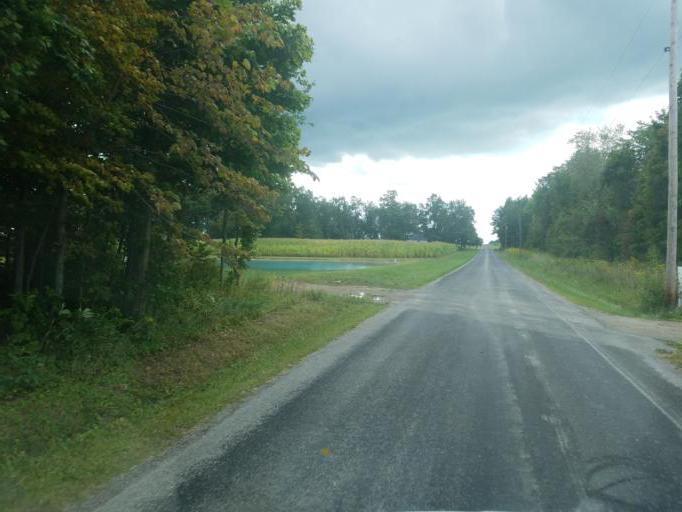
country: US
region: Ohio
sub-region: Huron County
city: Greenwich
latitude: 40.9831
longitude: -82.5348
